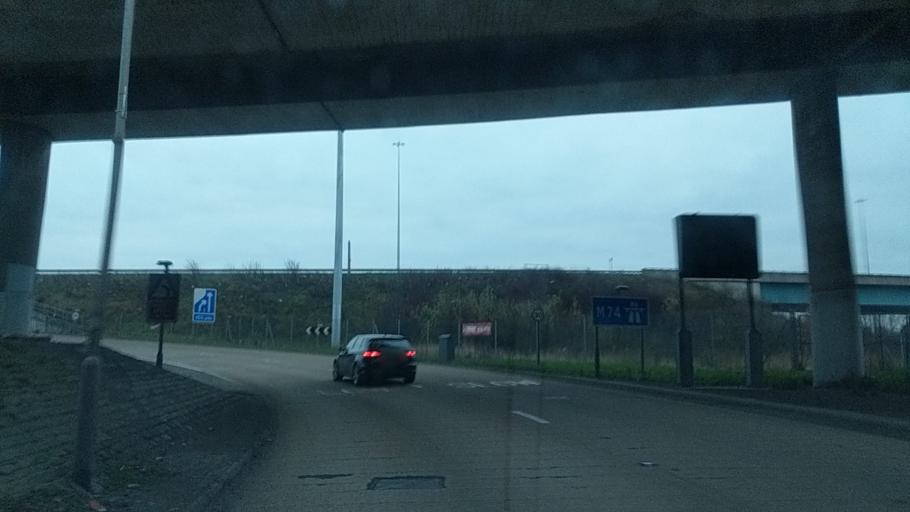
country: GB
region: Scotland
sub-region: Glasgow City
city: Glasgow
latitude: 55.8522
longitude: -4.2694
